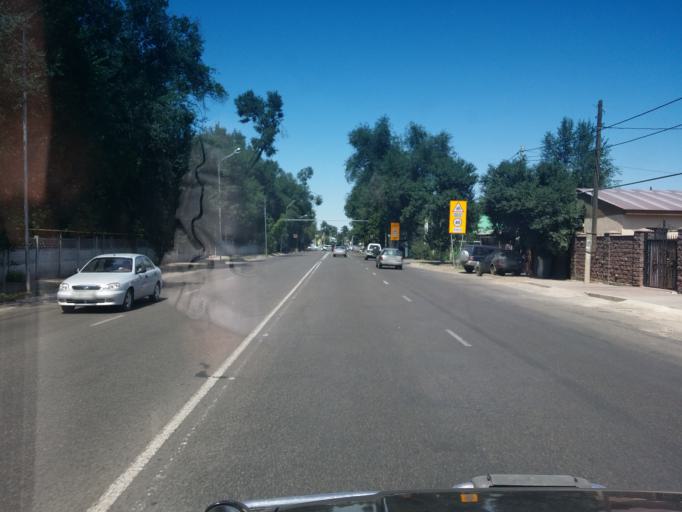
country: KZ
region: Almaty Qalasy
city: Almaty
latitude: 43.3113
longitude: 76.9306
